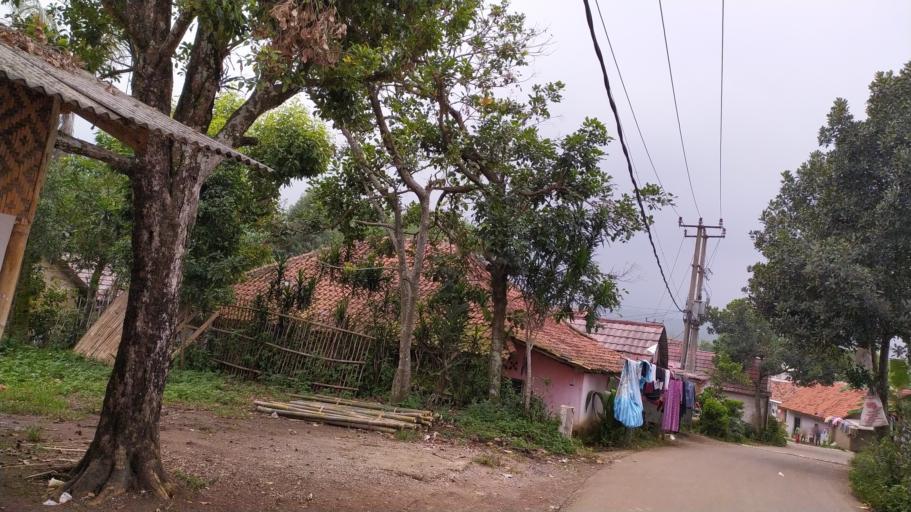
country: ID
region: West Java
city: Ciampea
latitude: -6.6306
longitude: 106.7051
